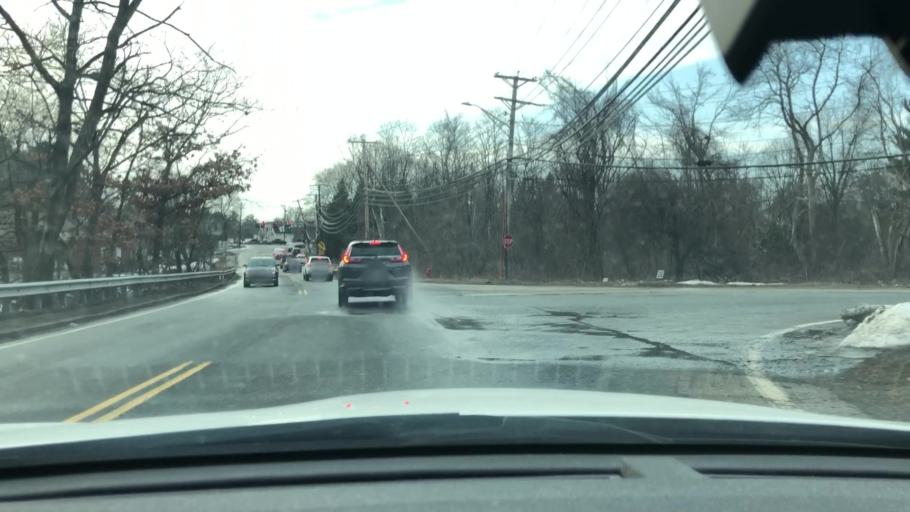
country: US
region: Massachusetts
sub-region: Middlesex County
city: Chelmsford
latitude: 42.5988
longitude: -71.3381
